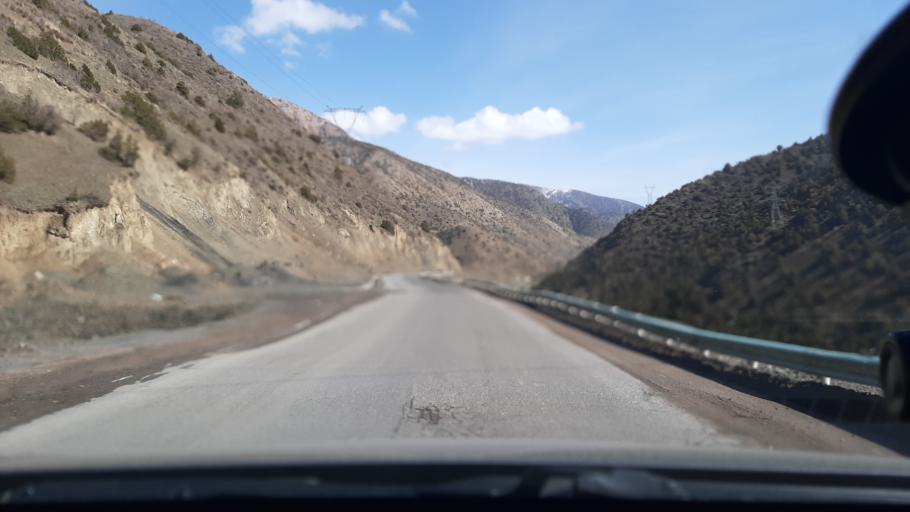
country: TJ
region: Viloyati Sughd
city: Ayni
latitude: 39.5666
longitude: 68.5901
